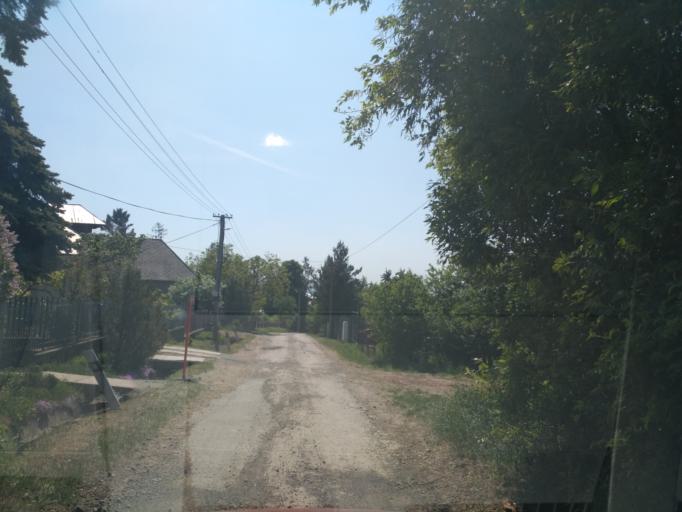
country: SK
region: Kosicky
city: Kosice
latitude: 48.8297
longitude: 21.4506
